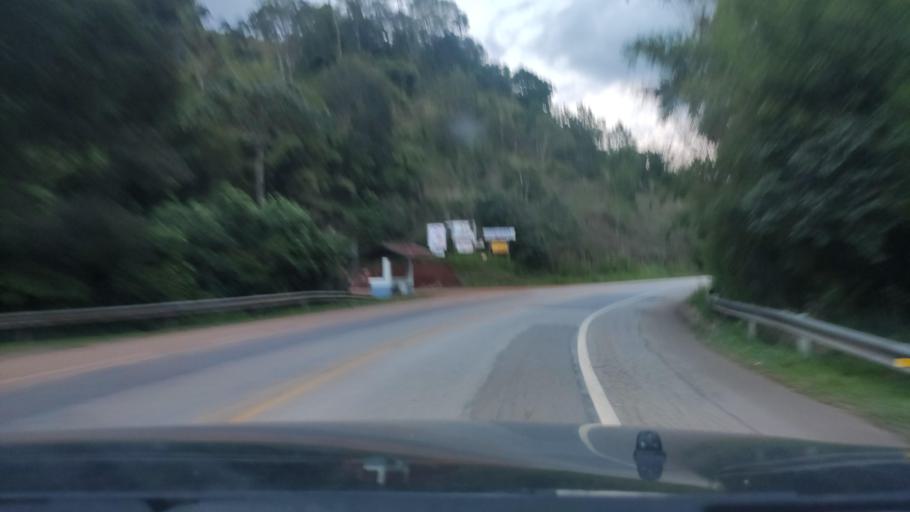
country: BR
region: Sao Paulo
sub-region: Campos Do Jordao
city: Campos do Jordao
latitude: -22.7976
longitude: -45.7498
